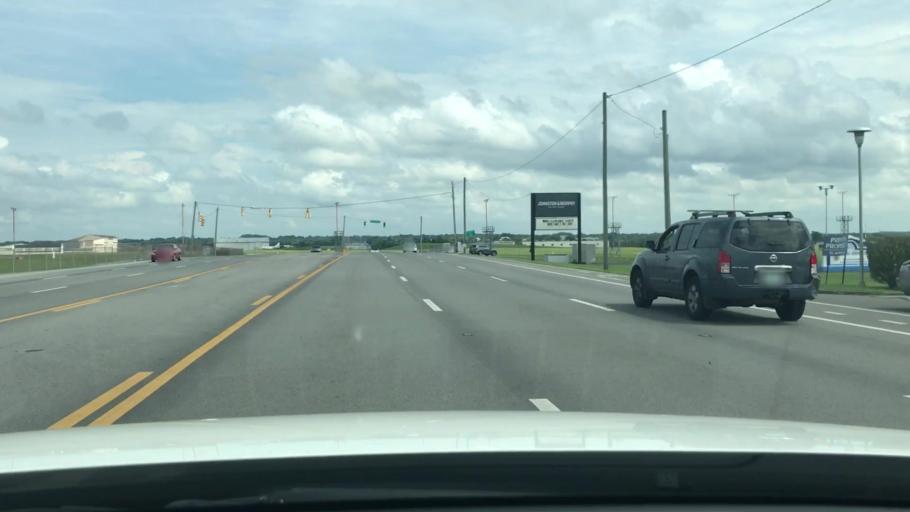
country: US
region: Tennessee
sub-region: Davidson County
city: Oak Hill
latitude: 36.1134
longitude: -86.6903
